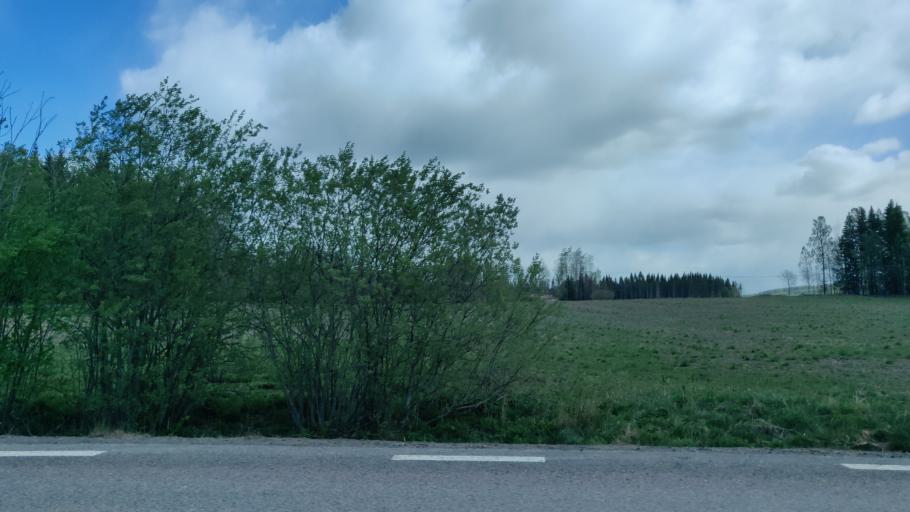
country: SE
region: Vaermland
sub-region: Karlstads Kommun
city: Molkom
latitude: 59.6105
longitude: 13.7360
